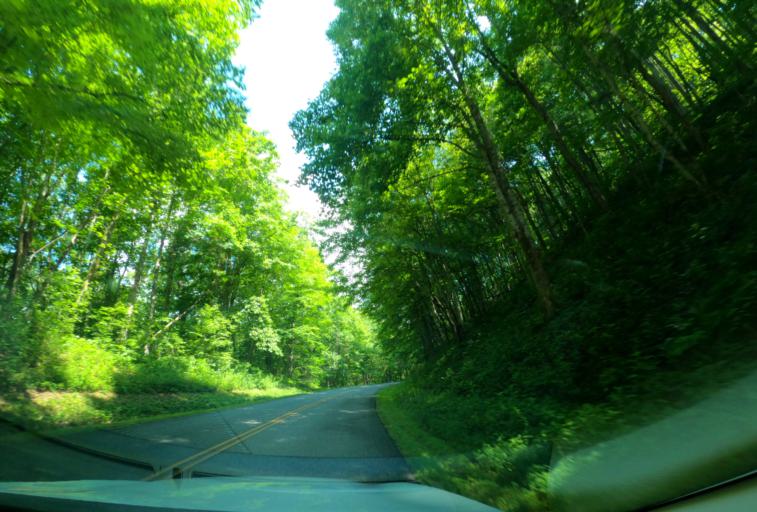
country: US
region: North Carolina
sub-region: Haywood County
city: Hazelwood
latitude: 35.4359
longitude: -83.0799
